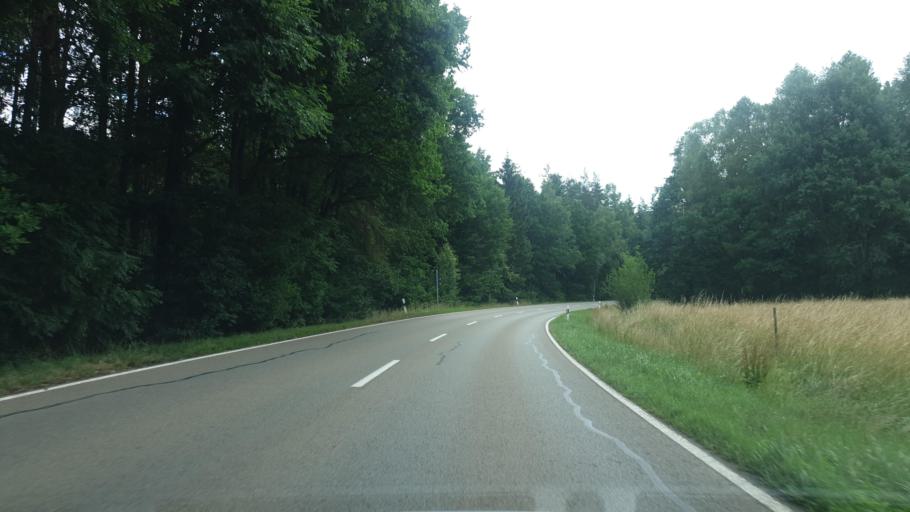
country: DE
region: Saxony
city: Pohl
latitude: 50.5671
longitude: 12.2052
